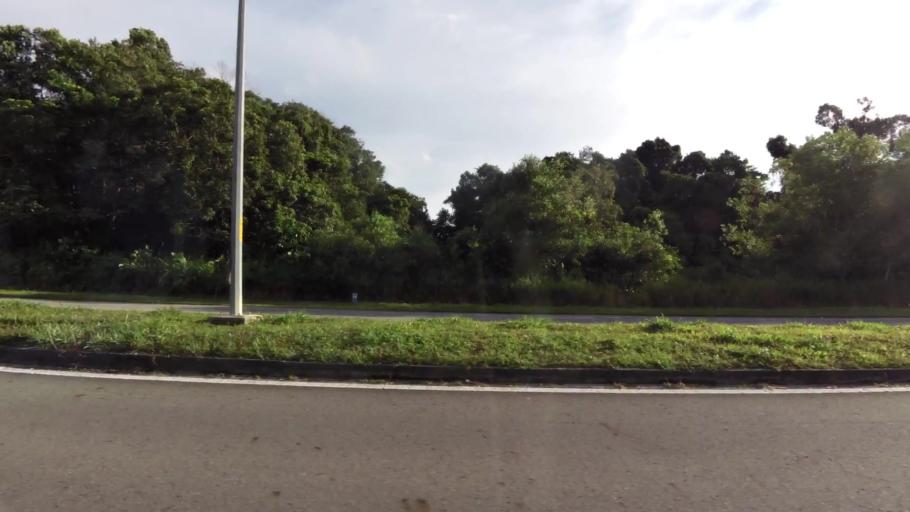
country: BN
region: Brunei and Muara
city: Bandar Seri Begawan
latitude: 4.9701
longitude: 114.9817
